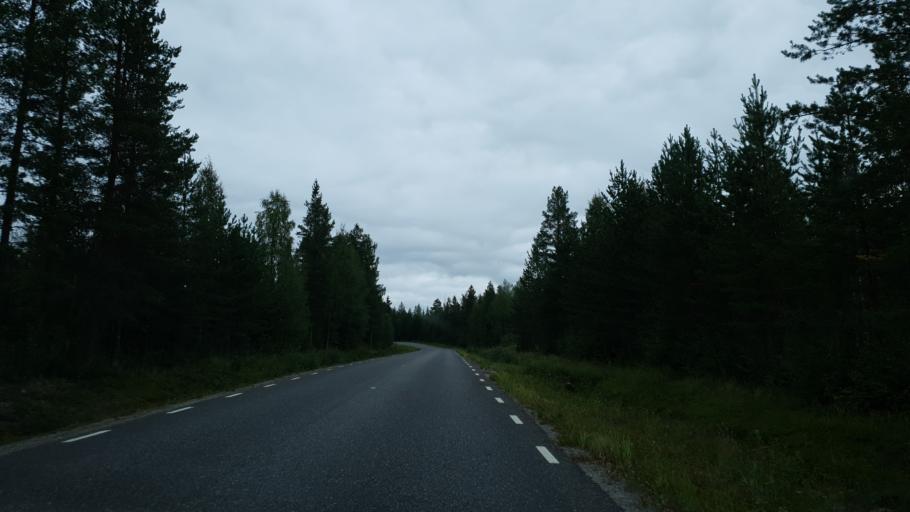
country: SE
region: Vaesterbotten
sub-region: Skelleftea Kommun
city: Viken
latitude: 64.8057
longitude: 20.7470
